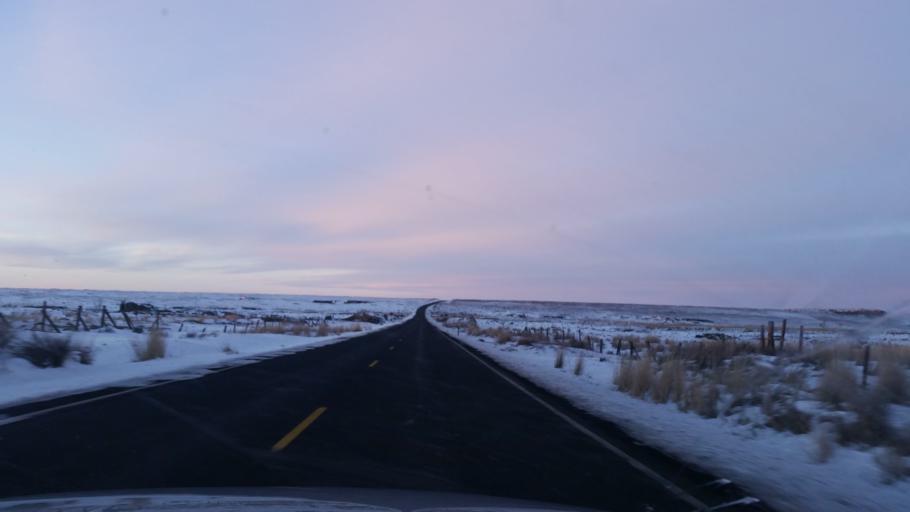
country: US
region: Washington
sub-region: Spokane County
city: Medical Lake
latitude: 47.2273
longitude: -117.9079
